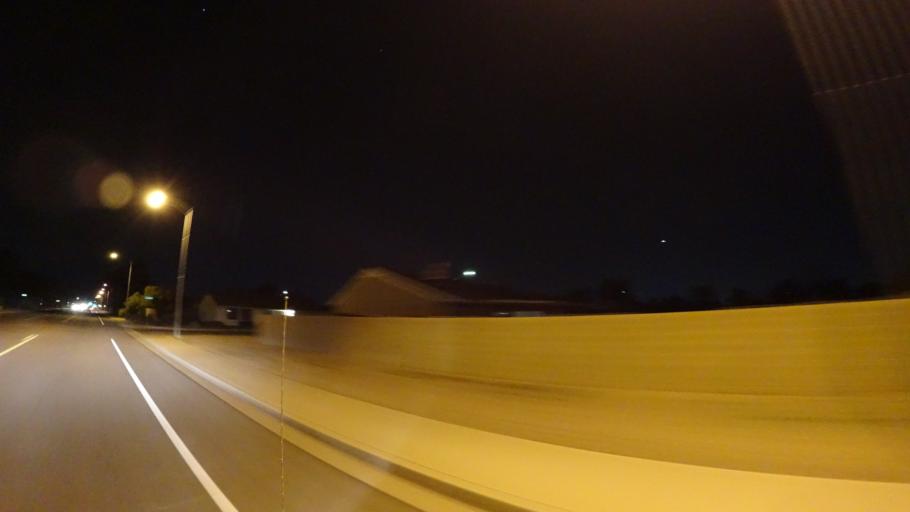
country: US
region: Arizona
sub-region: Maricopa County
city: Mesa
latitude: 33.4417
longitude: -111.8139
